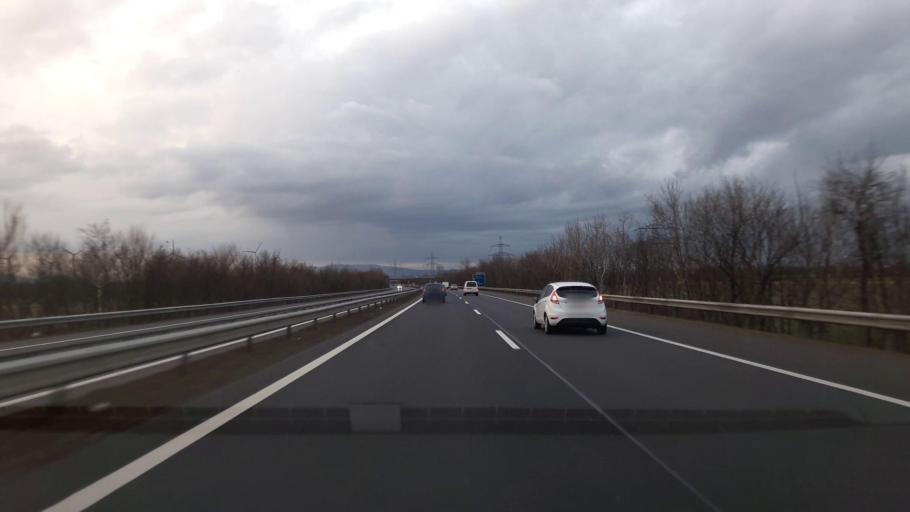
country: AT
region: Lower Austria
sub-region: Politischer Bezirk Baden
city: Pottendorf
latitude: 47.9173
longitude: 16.4048
